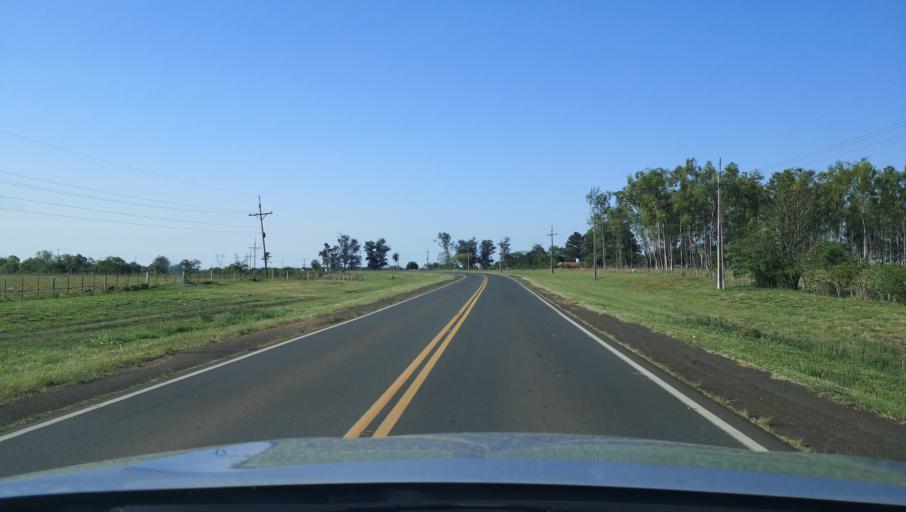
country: PY
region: Misiones
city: Santa Maria
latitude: -26.8093
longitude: -57.0209
